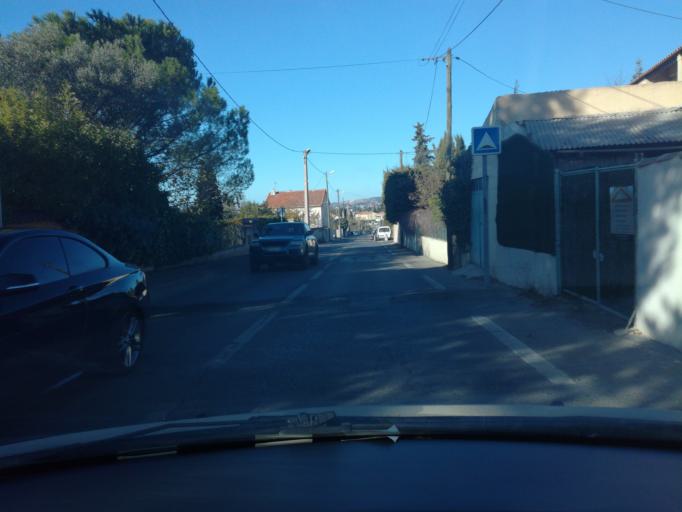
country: FR
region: Provence-Alpes-Cote d'Azur
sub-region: Departement des Bouches-du-Rhone
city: Allauch
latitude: 43.3299
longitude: 5.4725
